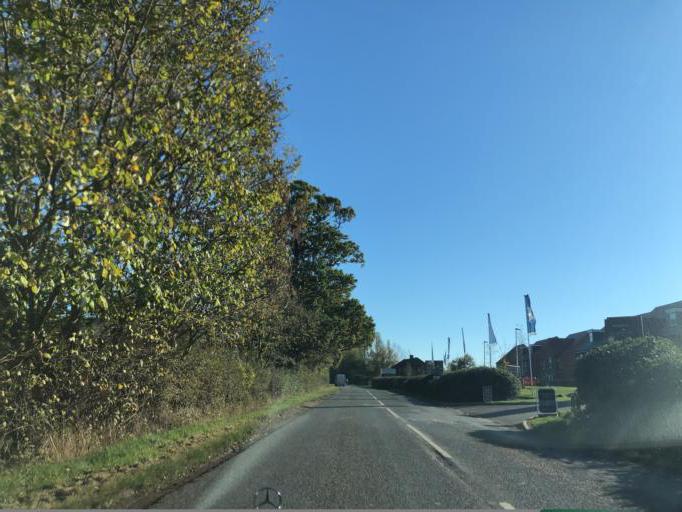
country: GB
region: England
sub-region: Warwickshire
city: Royal Leamington Spa
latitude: 52.2651
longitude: -1.5491
